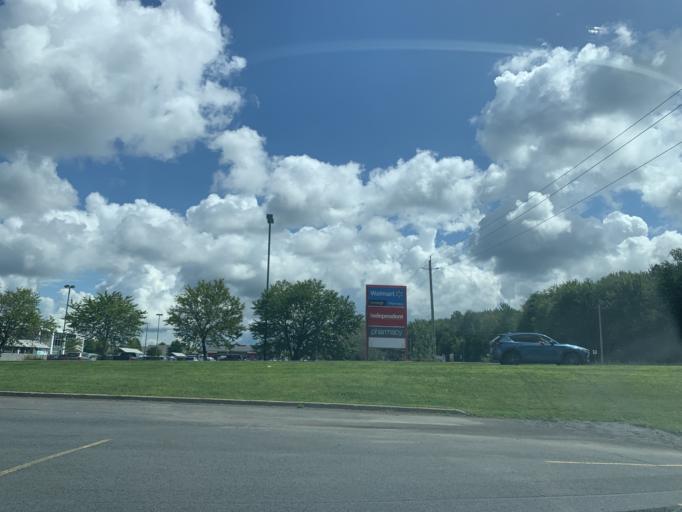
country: CA
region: Ontario
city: Hawkesbury
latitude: 45.5928
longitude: -74.6034
